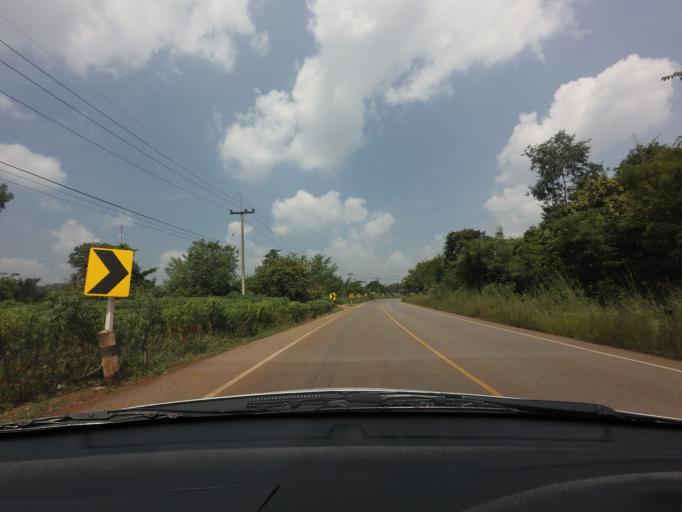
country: TH
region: Nakhon Ratchasima
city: Pak Chong
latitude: 14.5817
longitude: 101.5657
